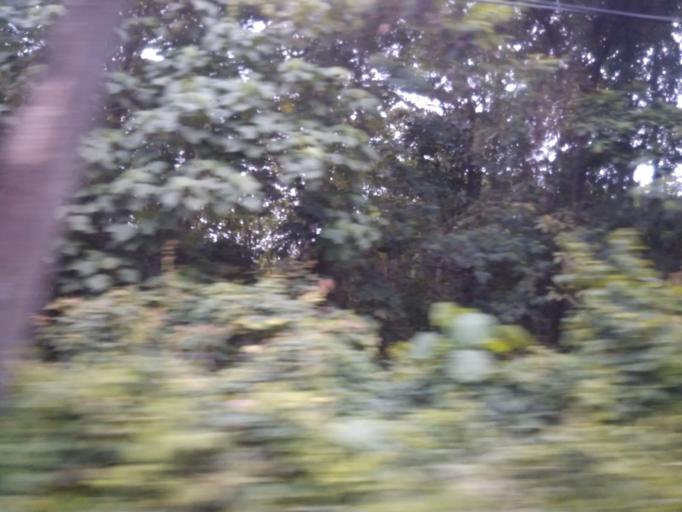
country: TH
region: Phuket
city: Mueang Phuket
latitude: 7.8144
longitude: 98.3995
